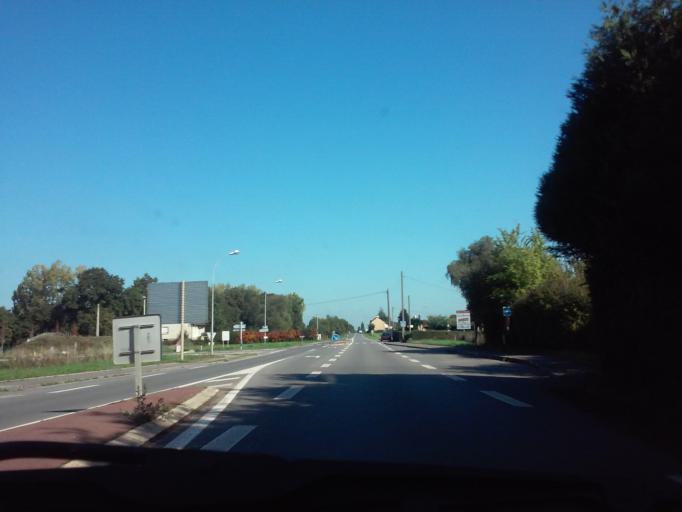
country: FR
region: Brittany
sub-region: Departement d'Ille-et-Vilaine
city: Betton
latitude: 48.1617
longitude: -1.6477
